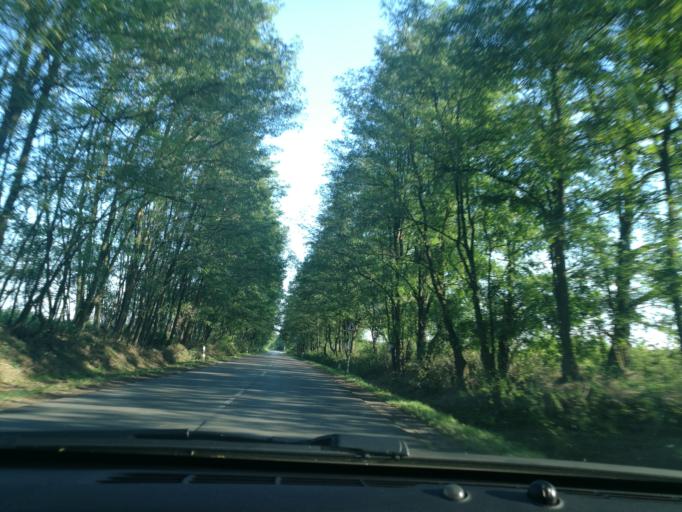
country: HU
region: Szabolcs-Szatmar-Bereg
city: Buj
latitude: 48.0759
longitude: 21.6403
